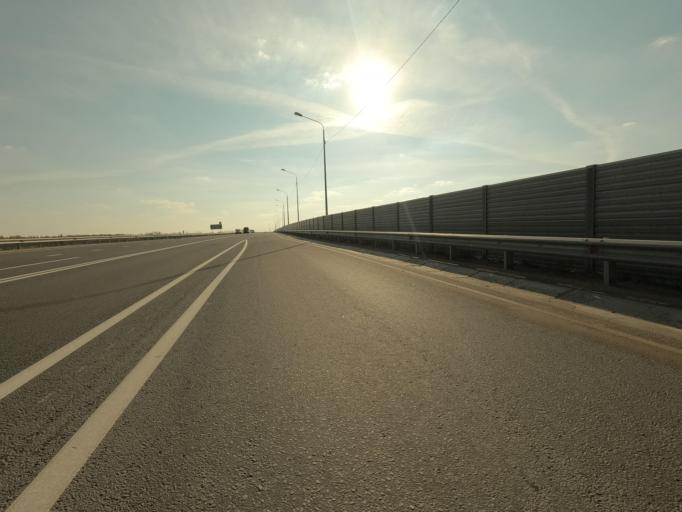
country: RU
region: Leningrad
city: Mga
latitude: 59.7564
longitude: 31.0931
